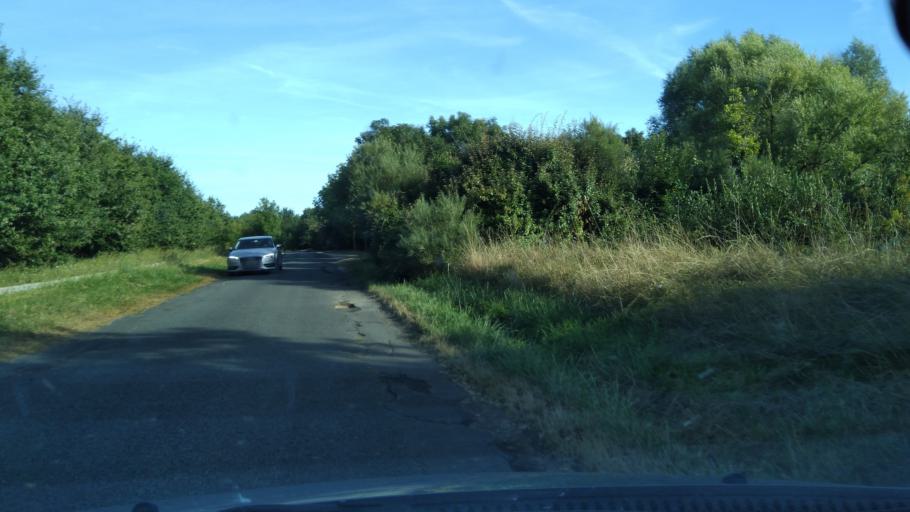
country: FR
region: Poitou-Charentes
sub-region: Departement de la Charente-Maritime
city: Dolus-d'Oleron
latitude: 45.9490
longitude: -1.3475
